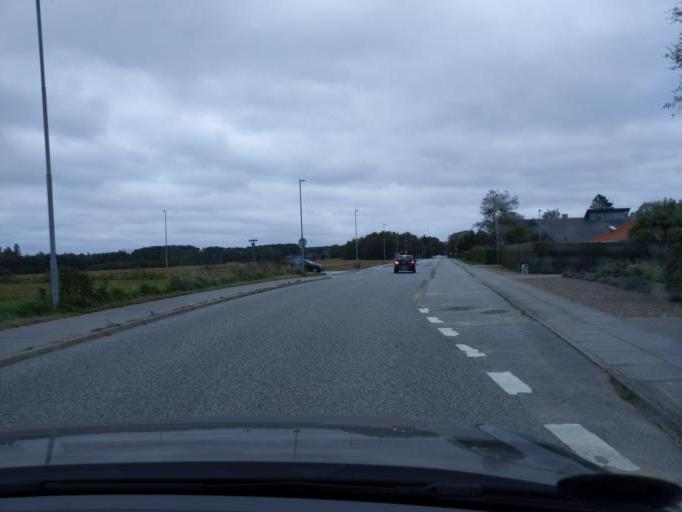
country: DK
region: Central Jutland
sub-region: Randers Kommune
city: Randers
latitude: 56.4775
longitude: 9.9922
